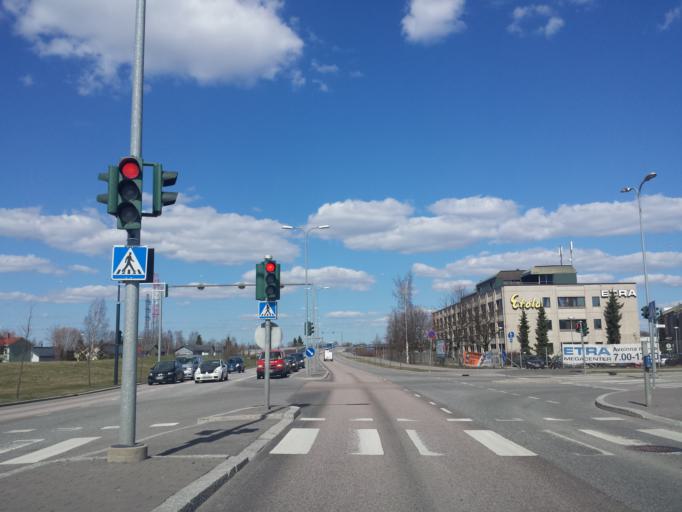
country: FI
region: Uusimaa
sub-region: Helsinki
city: Vantaa
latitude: 60.2822
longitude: 25.0122
